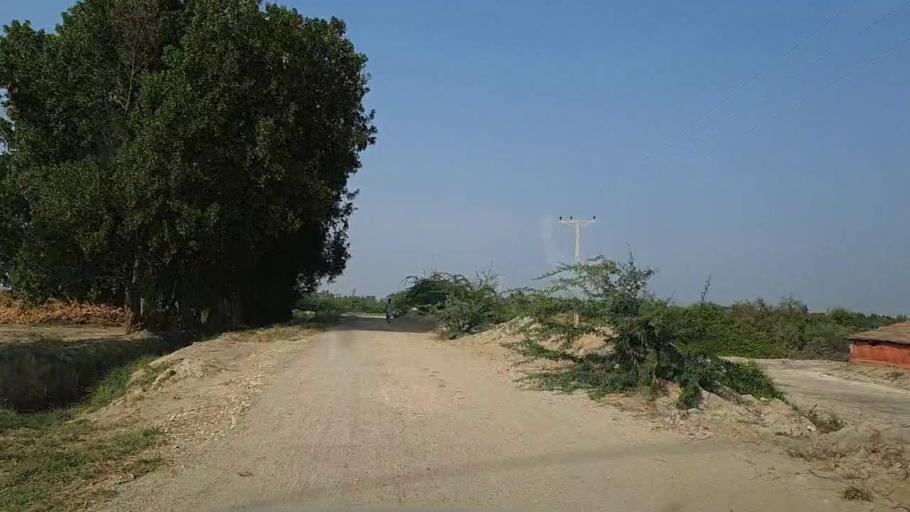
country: PK
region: Sindh
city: Mirpur Sakro
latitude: 24.5863
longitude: 67.5683
